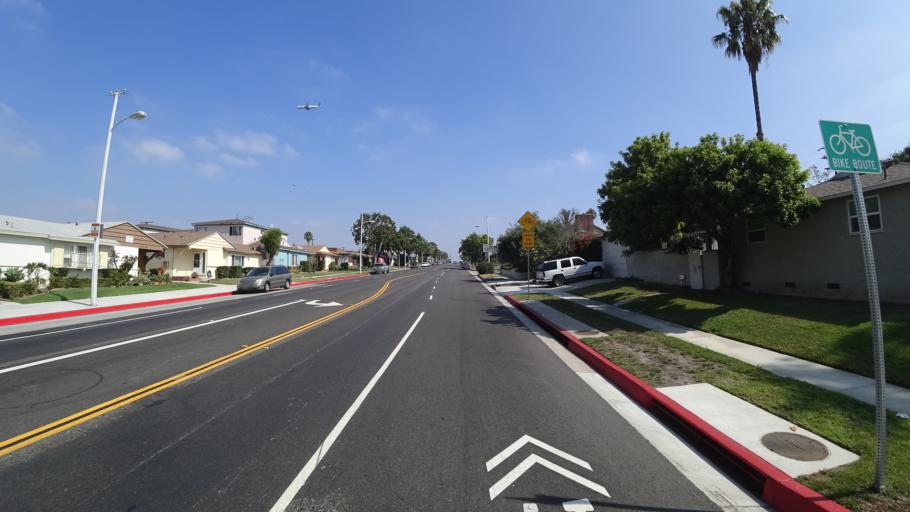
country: US
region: California
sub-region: Los Angeles County
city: Westmont
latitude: 33.9383
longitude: -118.3177
